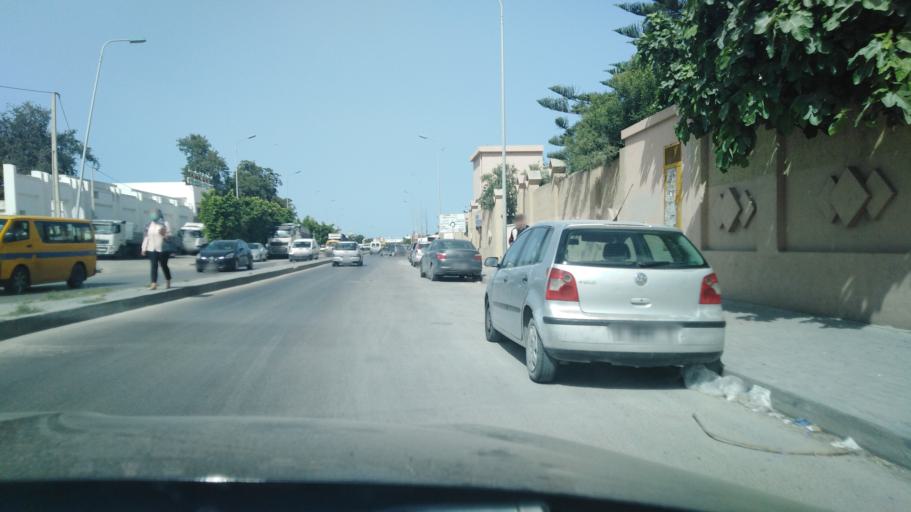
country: TN
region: Susah
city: Sousse
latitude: 35.8117
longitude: 10.6264
